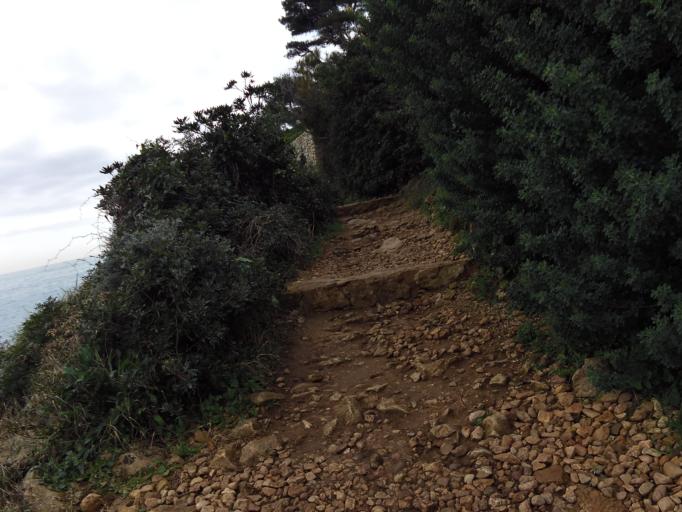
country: FR
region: Provence-Alpes-Cote d'Azur
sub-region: Departement des Alpes-Maritimes
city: Antibes
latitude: 43.5533
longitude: 7.1428
